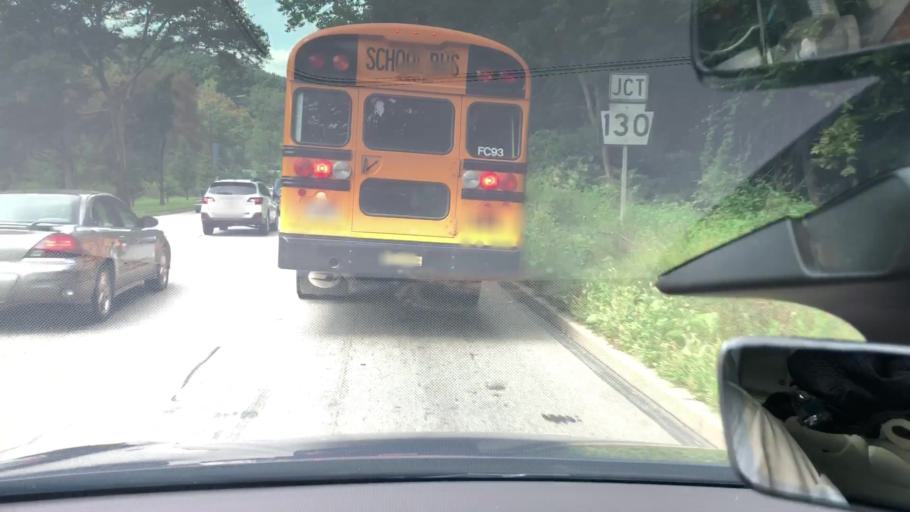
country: US
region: Pennsylvania
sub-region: Allegheny County
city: Aspinwall
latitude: 40.4809
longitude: -79.9078
